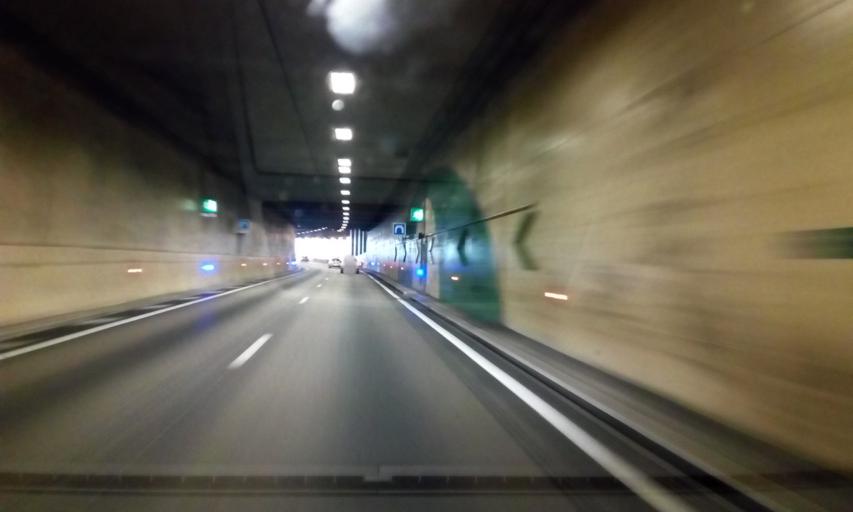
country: FR
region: Provence-Alpes-Cote d'Azur
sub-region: Departement du Var
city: Toulon
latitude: 43.1208
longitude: 5.9467
